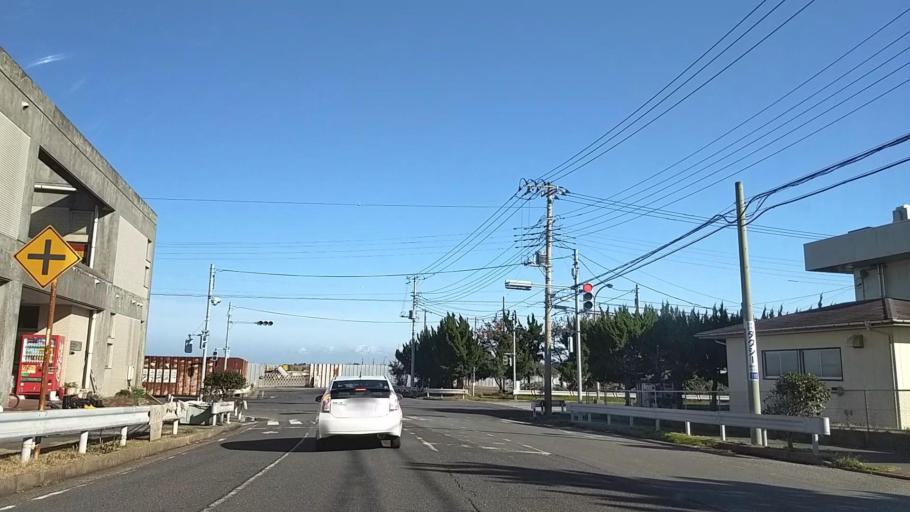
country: JP
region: Chiba
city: Hasaki
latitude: 35.7426
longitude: 140.8583
